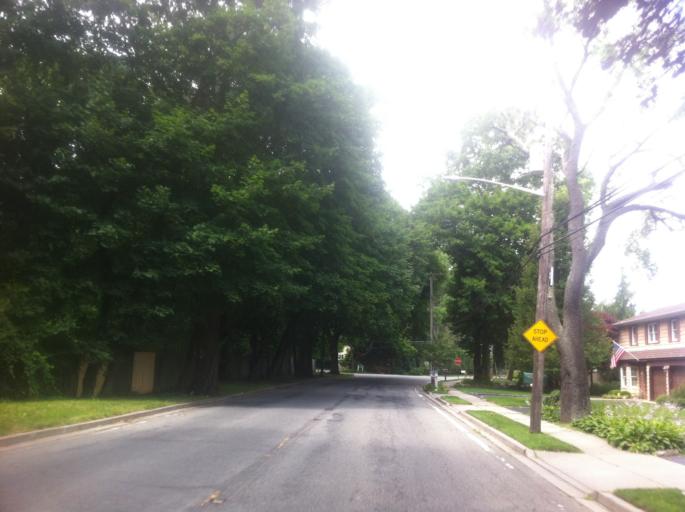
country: US
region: New York
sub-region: Nassau County
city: Locust Valley
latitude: 40.8539
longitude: -73.5959
